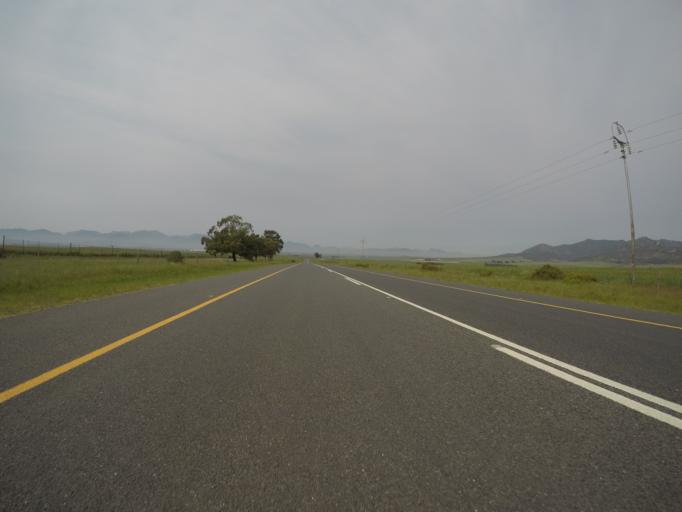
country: ZA
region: Western Cape
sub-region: West Coast District Municipality
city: Malmesbury
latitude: -33.5307
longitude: 18.8506
